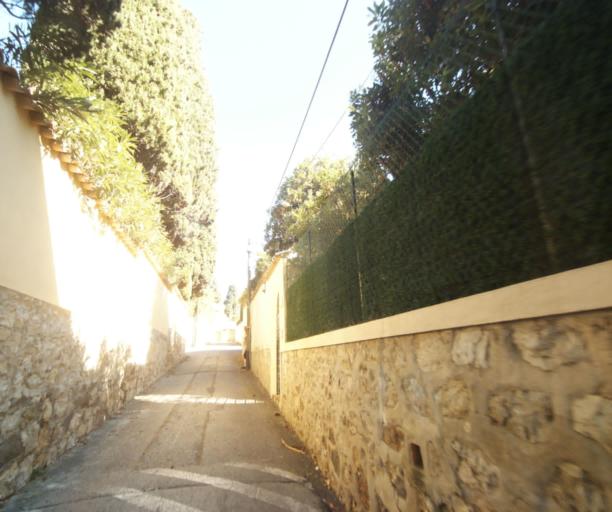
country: FR
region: Provence-Alpes-Cote d'Azur
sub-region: Departement des Alpes-Maritimes
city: Antibes
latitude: 43.5609
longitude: 7.1206
